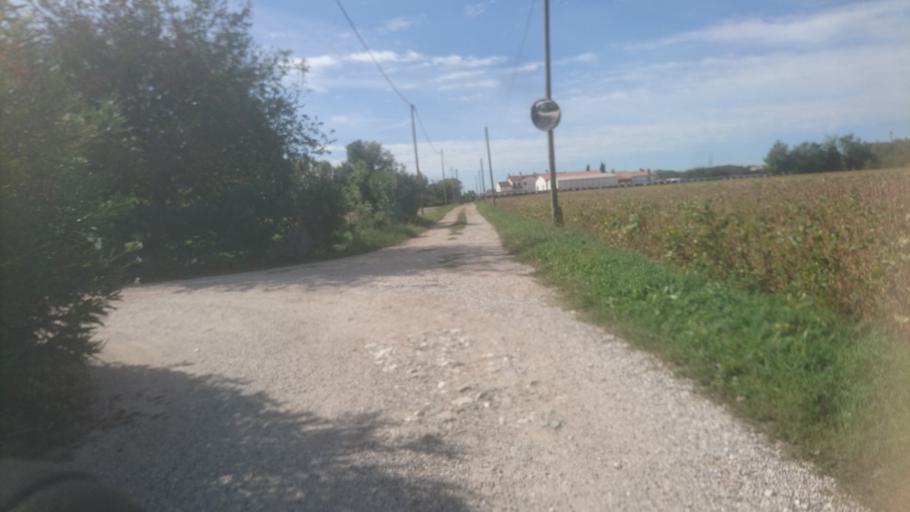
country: IT
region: Veneto
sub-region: Provincia di Padova
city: Veggiano
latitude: 45.4484
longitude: 11.7013
